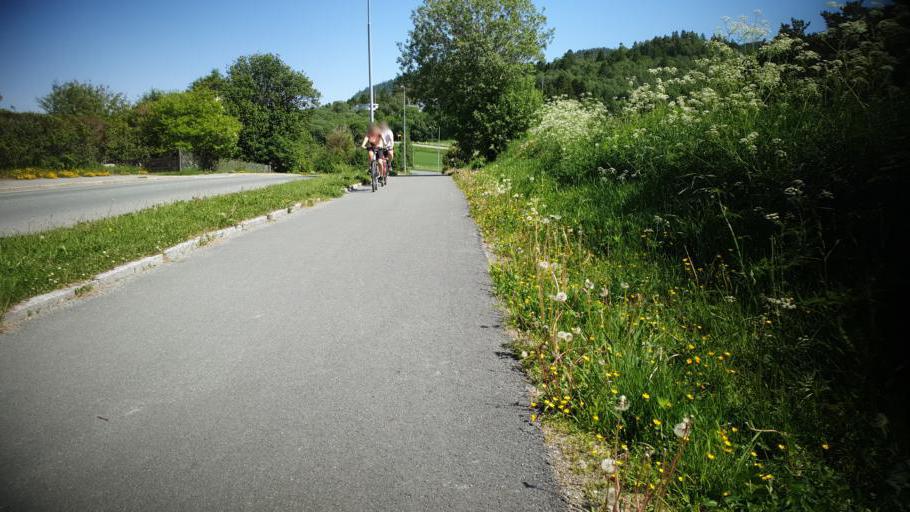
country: NO
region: Sor-Trondelag
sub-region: Malvik
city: Malvik
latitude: 63.4284
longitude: 10.5542
